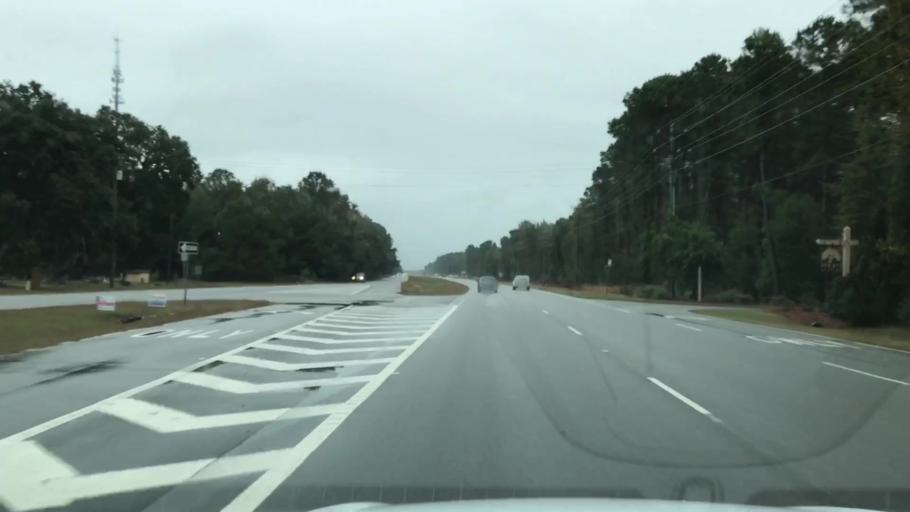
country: US
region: South Carolina
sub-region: Charleston County
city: Isle of Palms
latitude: 32.8970
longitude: -79.7339
